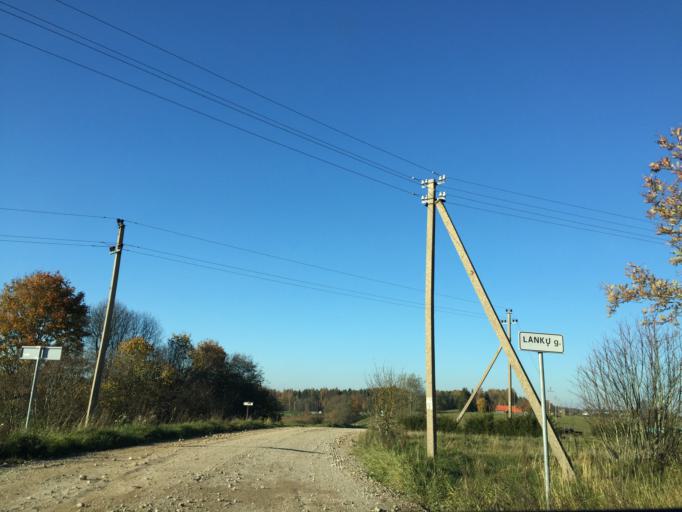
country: LT
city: Plateliai
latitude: 56.0704
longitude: 21.8571
